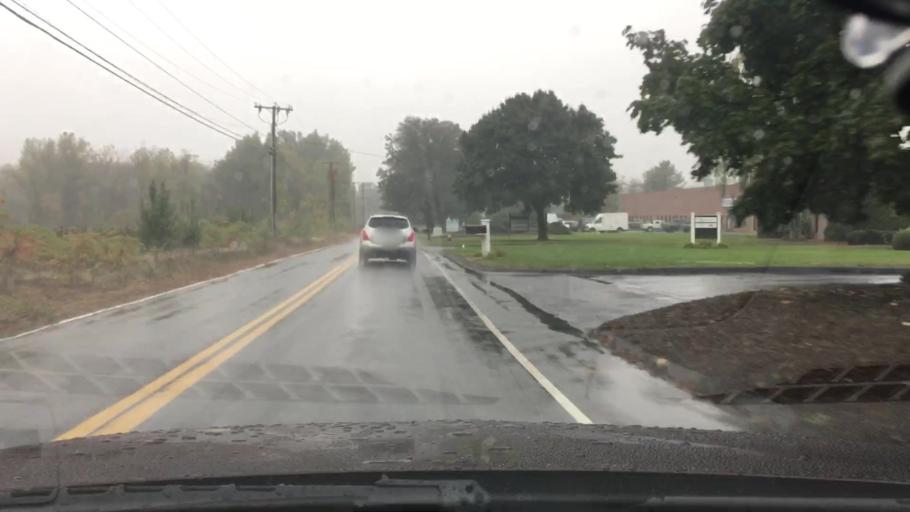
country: US
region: Connecticut
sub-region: Hartford County
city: Blue Hills
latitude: 41.8583
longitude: -72.7184
